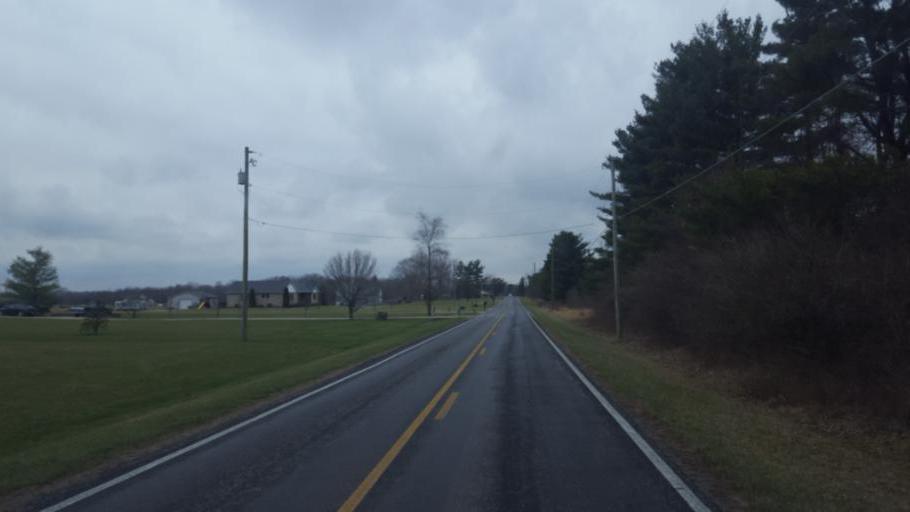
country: US
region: Ohio
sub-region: Delaware County
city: Delaware
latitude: 40.3537
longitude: -83.0573
